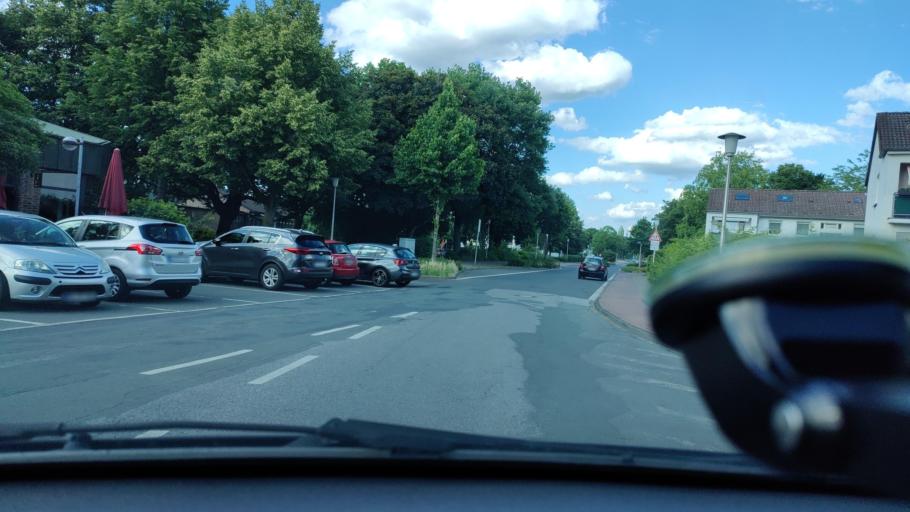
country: DE
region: North Rhine-Westphalia
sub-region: Regierungsbezirk Dusseldorf
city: Kamp-Lintfort
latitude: 51.5148
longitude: 6.5321
